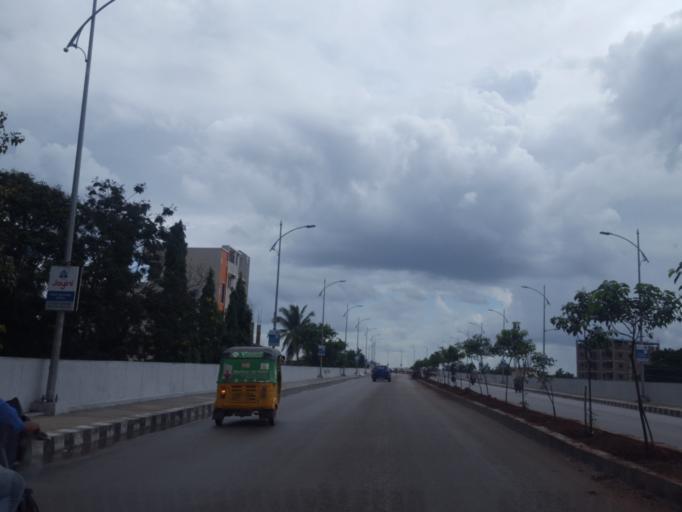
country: IN
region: Telangana
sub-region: Medak
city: Serilingampalle
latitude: 17.4849
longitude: 78.3125
